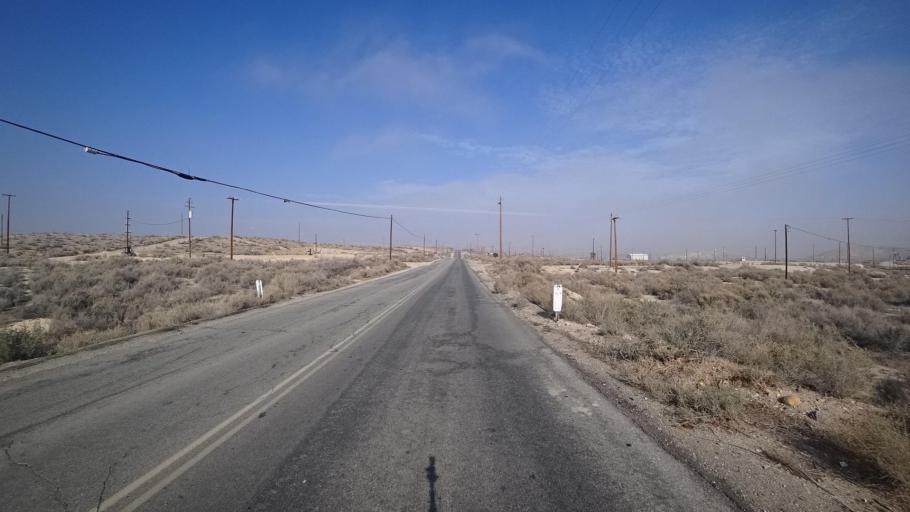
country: US
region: California
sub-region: Kern County
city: Ford City
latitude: 35.1739
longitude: -119.4653
